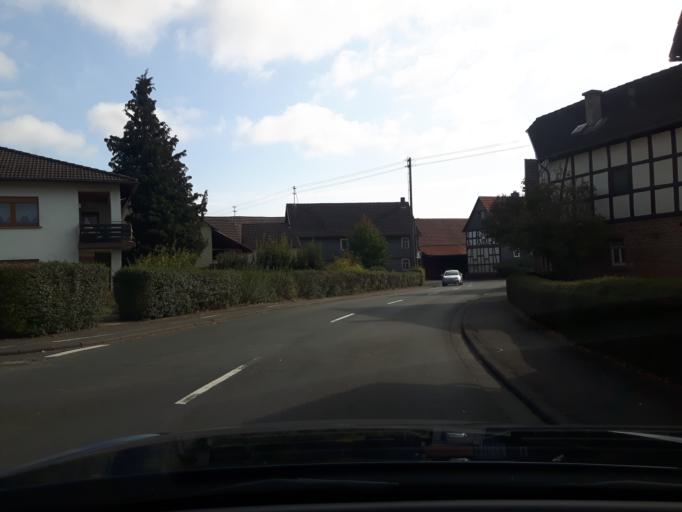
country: DE
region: Hesse
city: Battenberg
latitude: 50.9610
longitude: 8.6471
